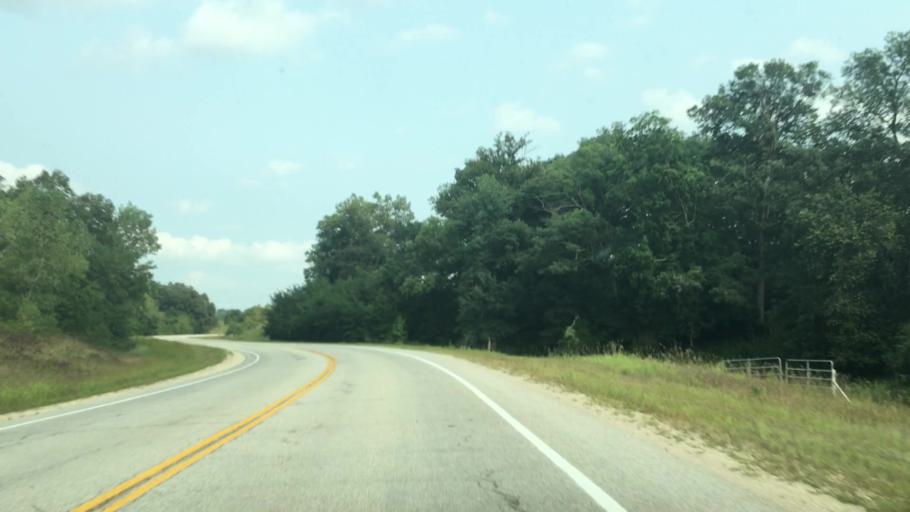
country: US
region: Minnesota
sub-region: Fillmore County
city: Preston
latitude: 43.6973
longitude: -91.9598
